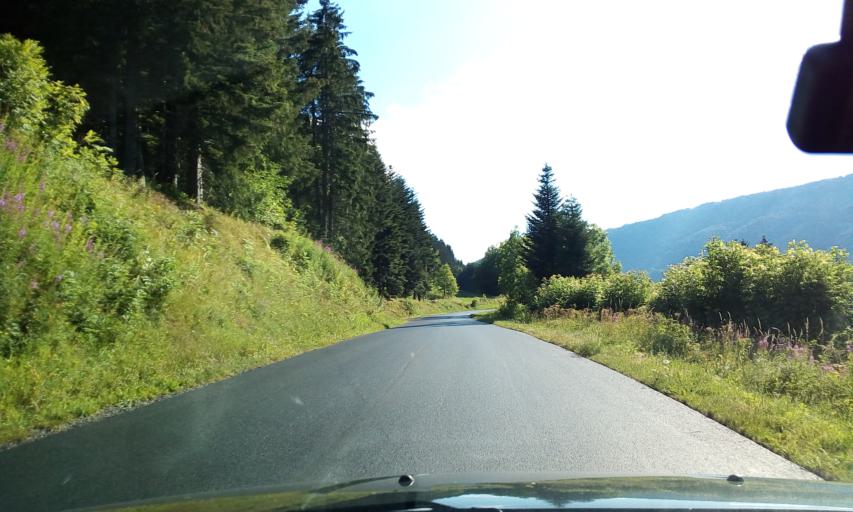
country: FR
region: Rhone-Alpes
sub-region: Departement de l'Isere
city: Lans-en-Vercors
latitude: 45.1625
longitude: 5.6250
